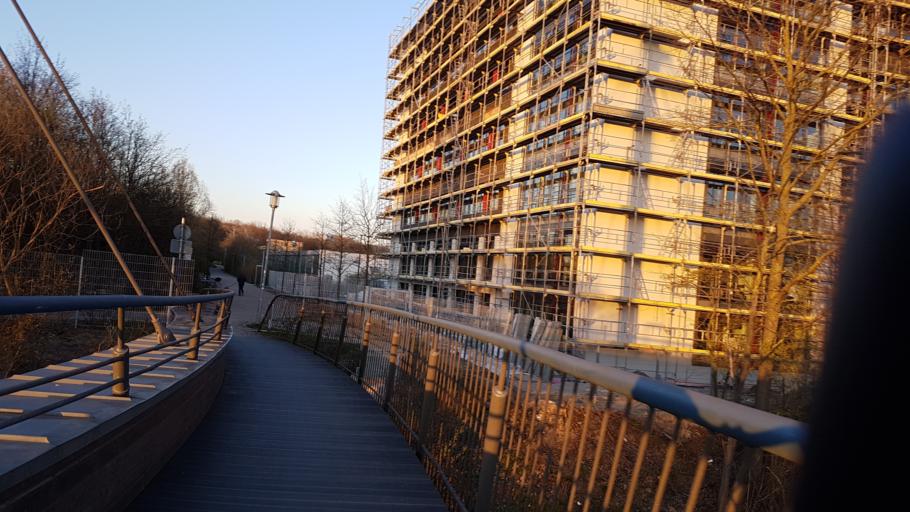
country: DE
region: Lower Saxony
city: Laatzen
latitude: 52.3116
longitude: 9.8020
